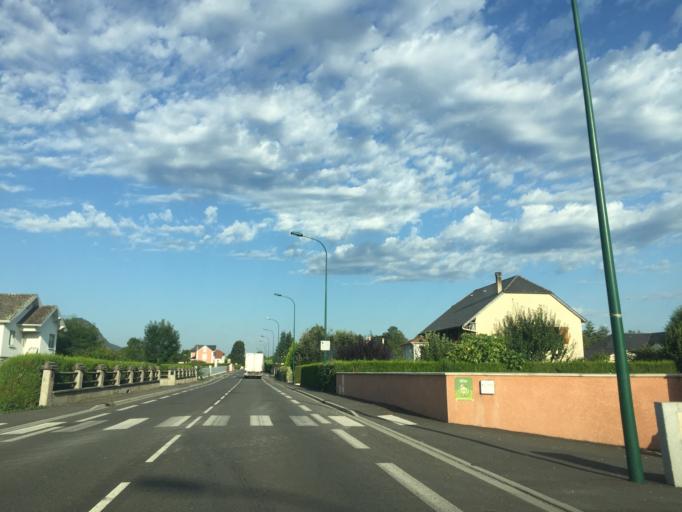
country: FR
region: Midi-Pyrenees
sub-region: Departement des Hautes-Pyrenees
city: Lourdes
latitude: 43.0957
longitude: -0.0194
